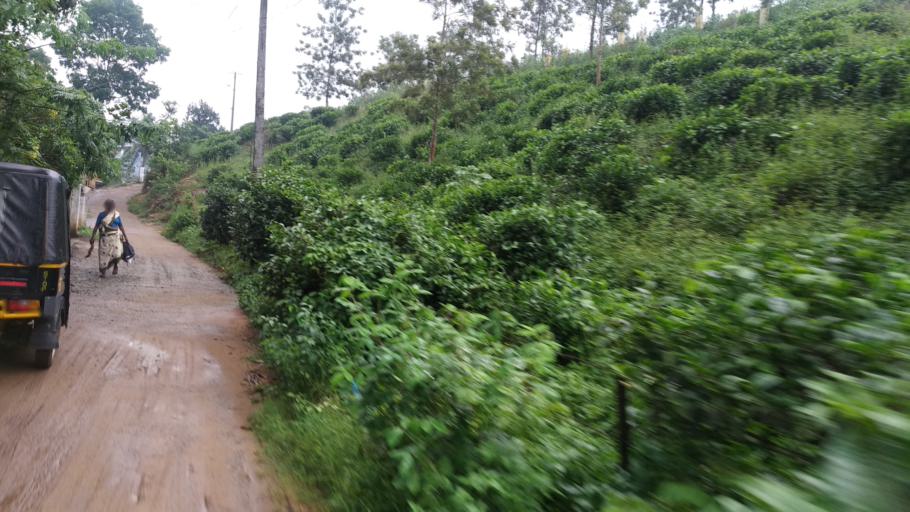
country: IN
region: Tamil Nadu
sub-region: Theni
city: Gudalur
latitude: 9.5666
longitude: 77.0852
